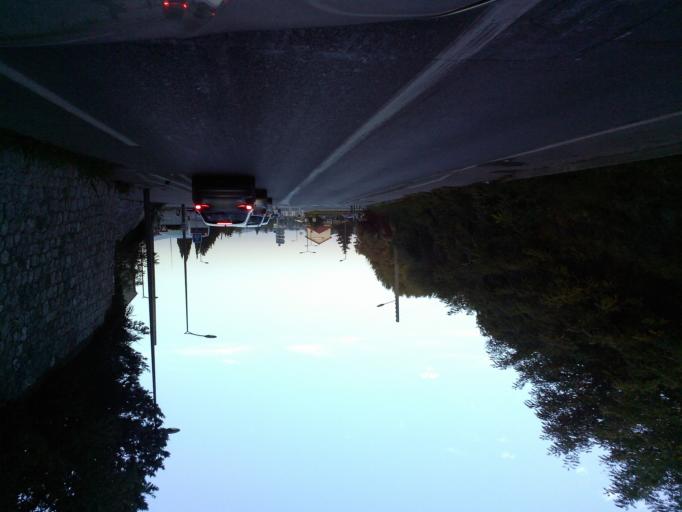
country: FR
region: Provence-Alpes-Cote d'Azur
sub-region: Departement des Bouches-du-Rhone
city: Lambesc
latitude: 43.6536
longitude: 5.2704
